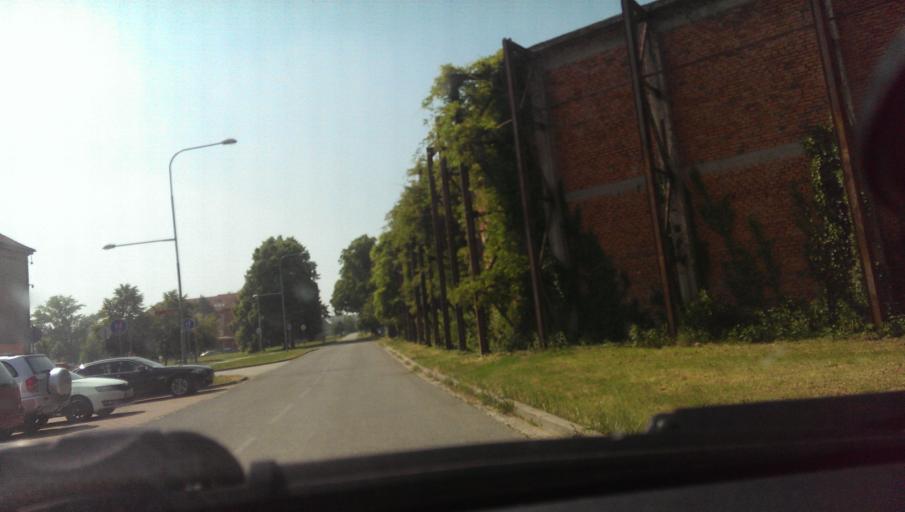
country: CZ
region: Zlin
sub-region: Okres Uherske Hradiste
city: Uherske Hradiste
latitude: 49.0714
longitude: 17.4709
